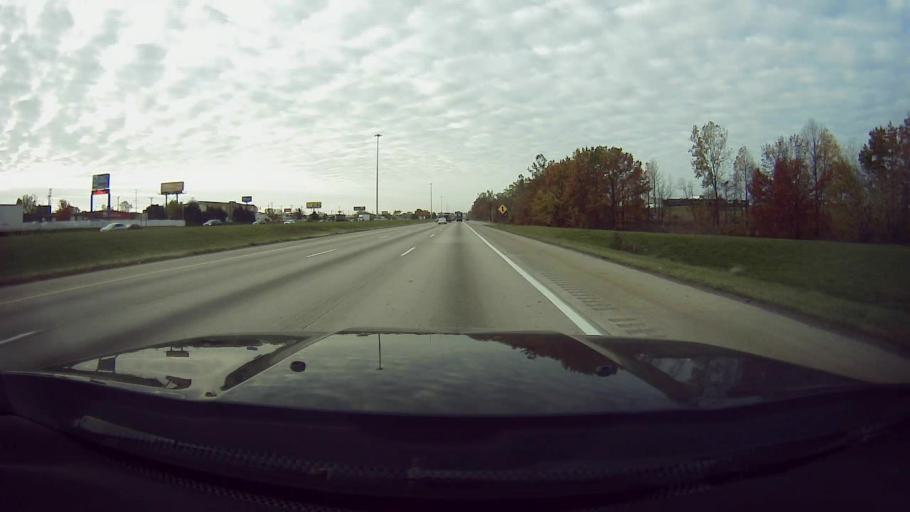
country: US
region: Michigan
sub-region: Wayne County
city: Melvindale
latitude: 42.2834
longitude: -83.1981
